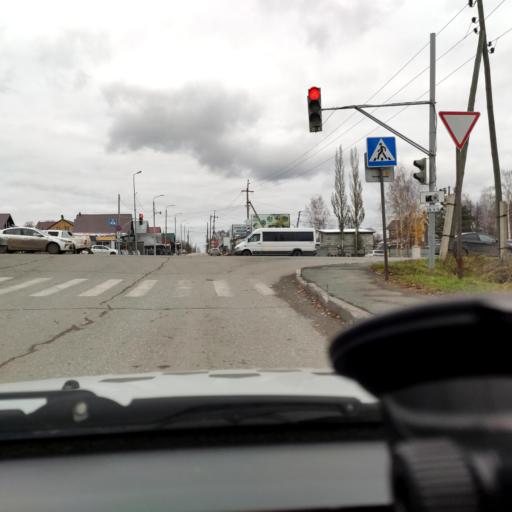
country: RU
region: Perm
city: Kondratovo
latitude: 58.0545
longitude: 56.1225
